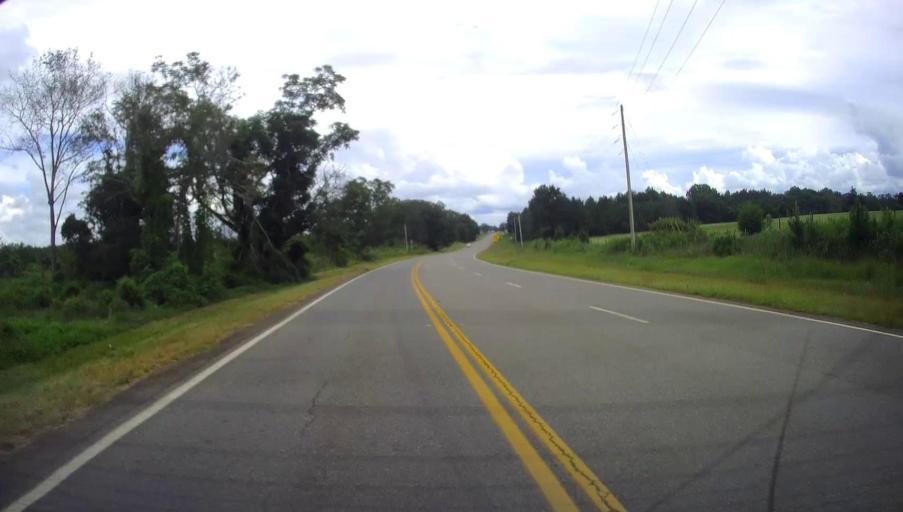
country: US
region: Georgia
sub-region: Schley County
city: Ellaville
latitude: 32.2548
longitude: -84.3417
